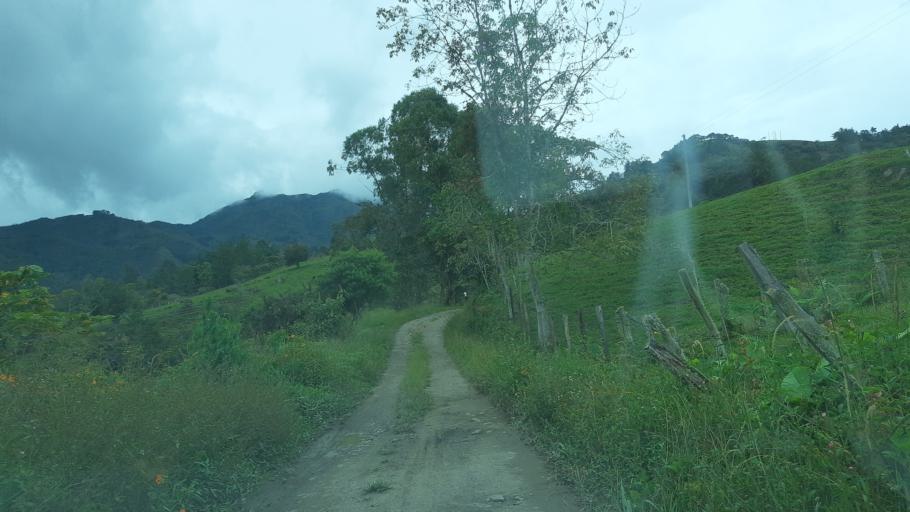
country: CO
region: Boyaca
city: Garagoa
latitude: 5.0837
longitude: -73.3535
